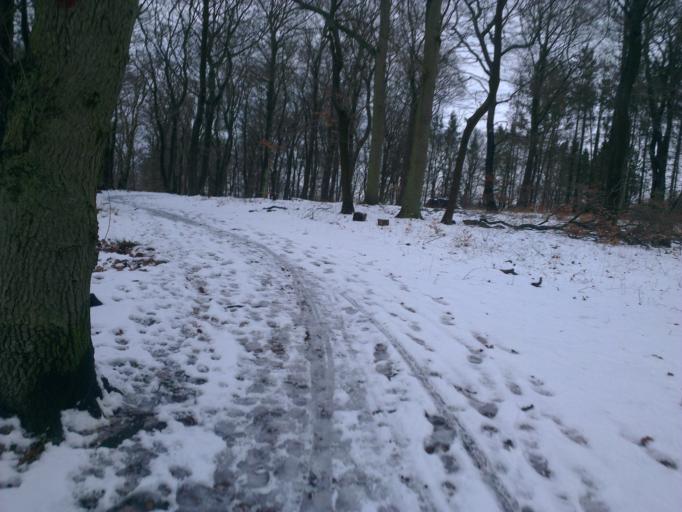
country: DK
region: Capital Region
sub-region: Frederikssund Kommune
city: Jaegerspris
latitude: 55.8515
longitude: 12.0123
